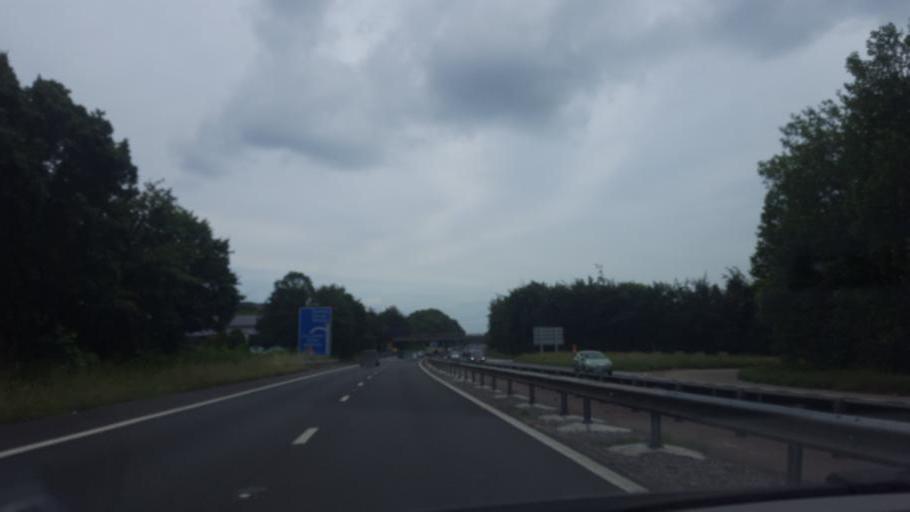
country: GB
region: England
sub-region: Royal Borough of Windsor and Maidenhead
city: Maidenhead
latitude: 51.5087
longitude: -0.7391
